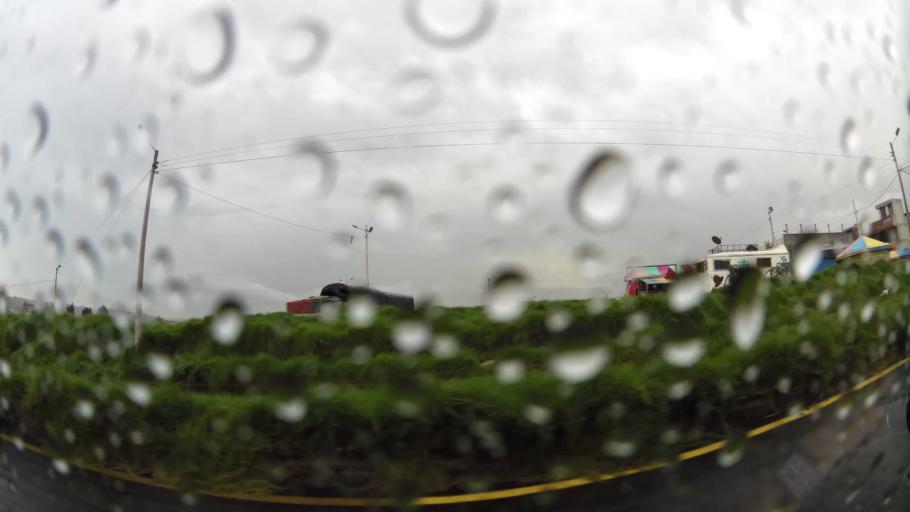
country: EC
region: Pichincha
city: Quito
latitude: -0.3101
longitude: -78.5479
